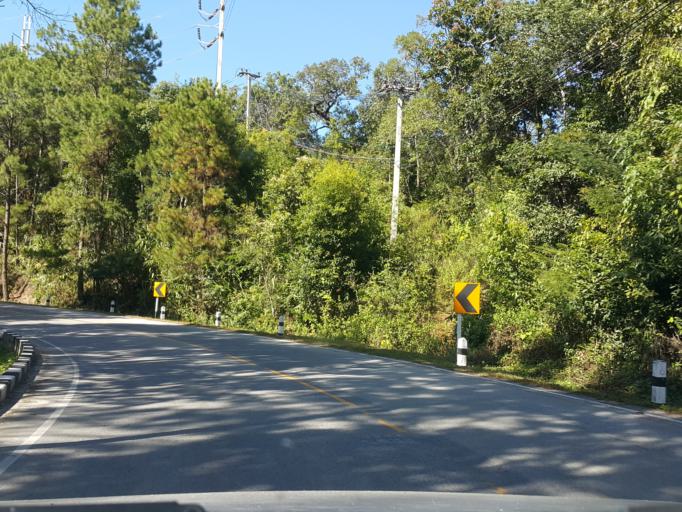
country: TH
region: Mae Hong Son
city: Mae Hi
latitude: 19.2692
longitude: 98.5809
